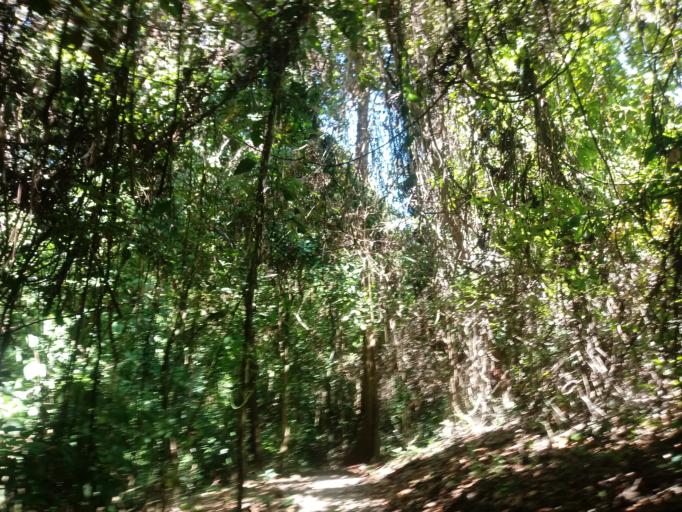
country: CR
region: Puntarenas
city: Paquera
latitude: 9.5859
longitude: -85.0945
